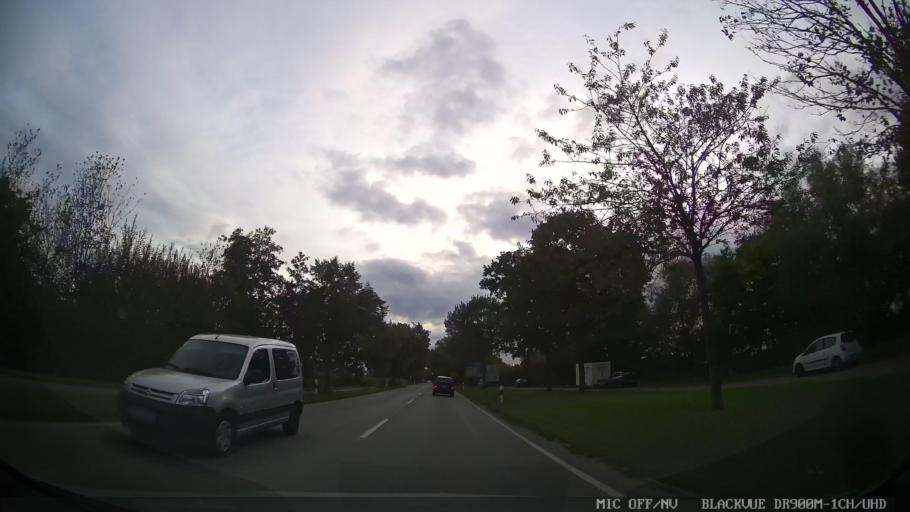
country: DE
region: Schleswig-Holstein
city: Altenkrempe
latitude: 54.1161
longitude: 10.8356
